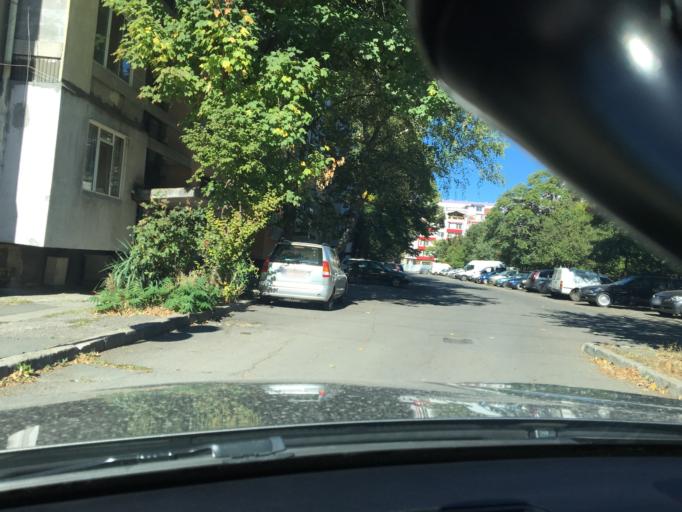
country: BG
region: Burgas
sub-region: Obshtina Burgas
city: Burgas
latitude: 42.5174
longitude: 27.4486
